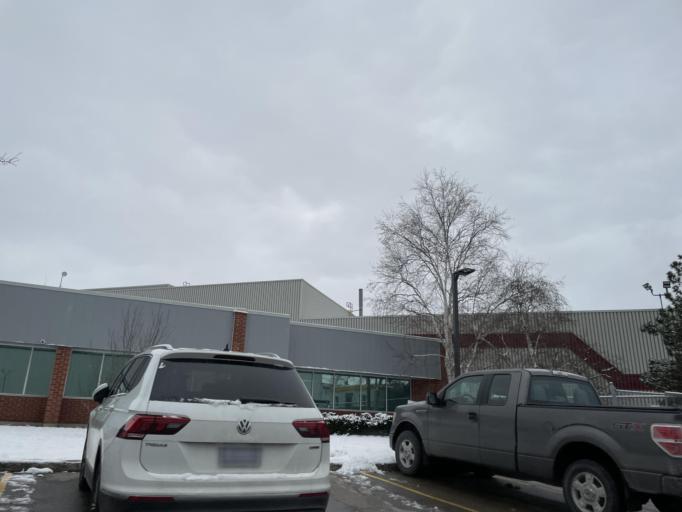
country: CA
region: Ontario
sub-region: Wellington County
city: Guelph
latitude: 43.5320
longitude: -80.3100
